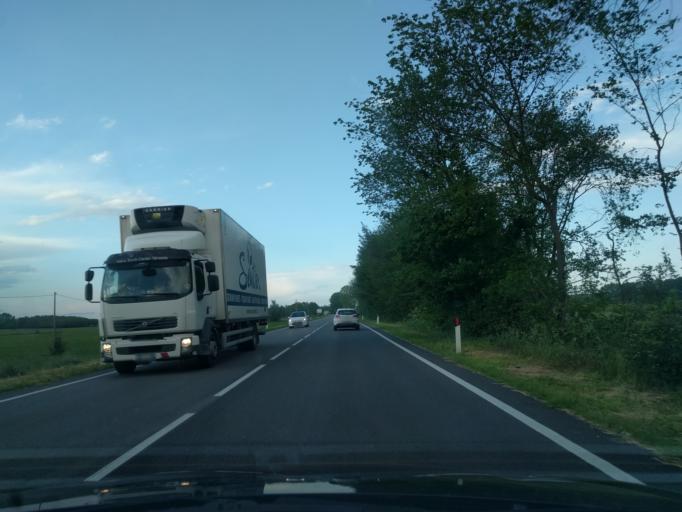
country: IT
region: Emilia-Romagna
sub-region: Provincia di Ferrara
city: Ro
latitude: 44.9362
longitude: 11.7290
